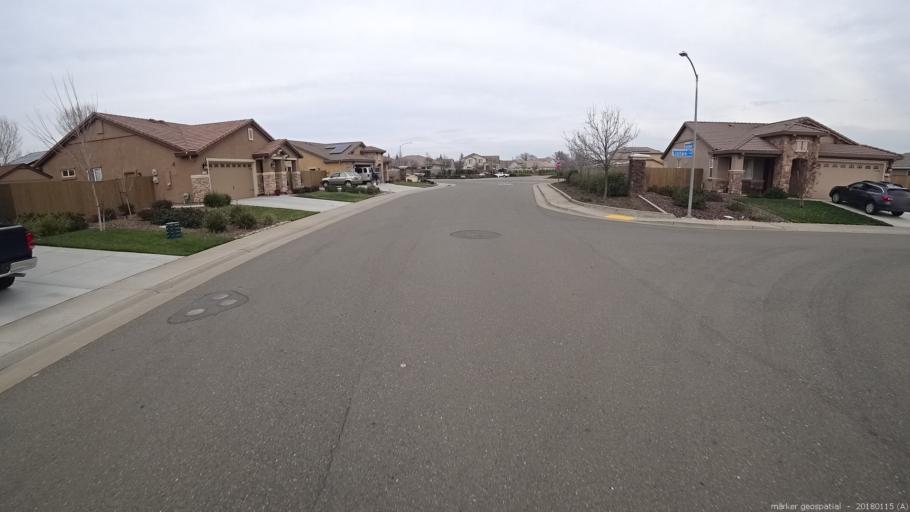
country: US
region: California
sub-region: Sacramento County
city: Rancho Cordova
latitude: 38.5791
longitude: -121.2685
